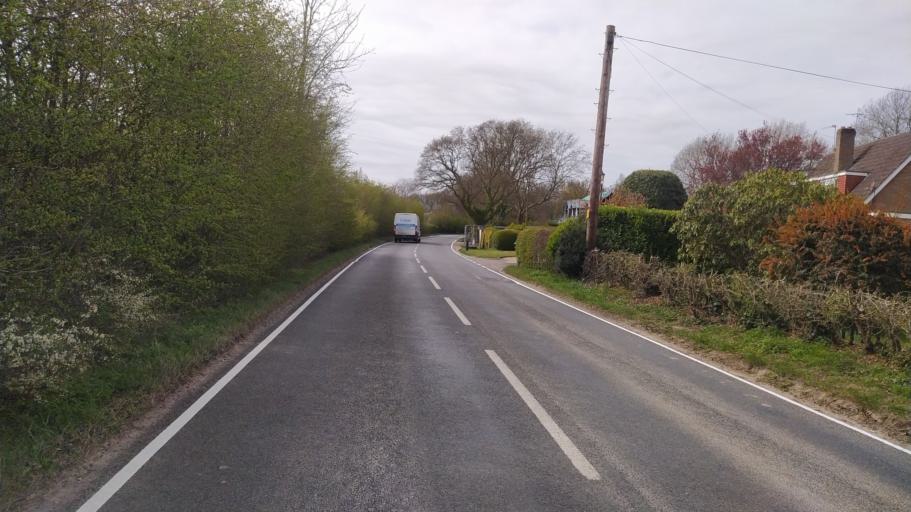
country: GB
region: England
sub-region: Hampshire
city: Wickham
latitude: 50.8998
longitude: -1.2048
